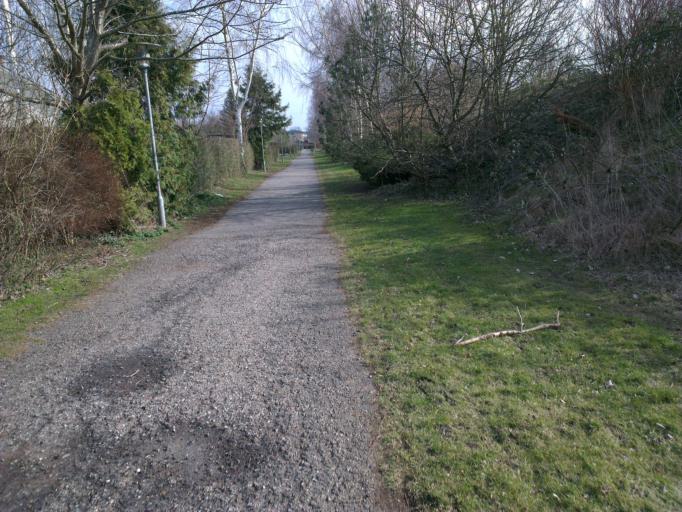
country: DK
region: Capital Region
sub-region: Egedal Kommune
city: Olstykke
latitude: 55.7978
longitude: 12.1533
